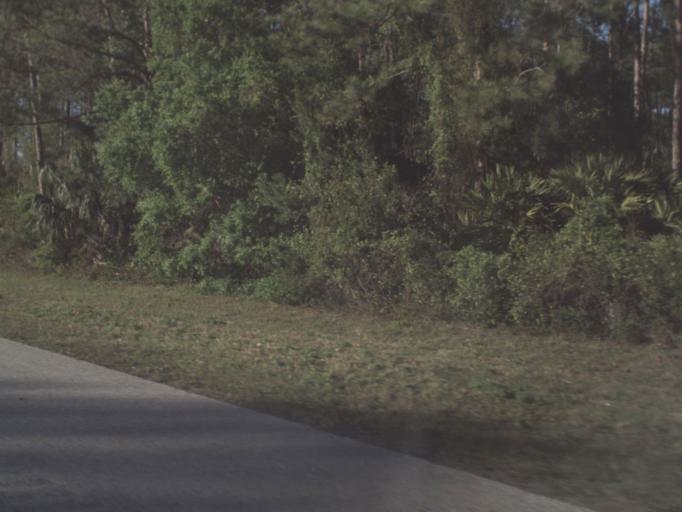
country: US
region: Florida
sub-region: Flagler County
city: Palm Coast
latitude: 29.5718
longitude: -81.2303
